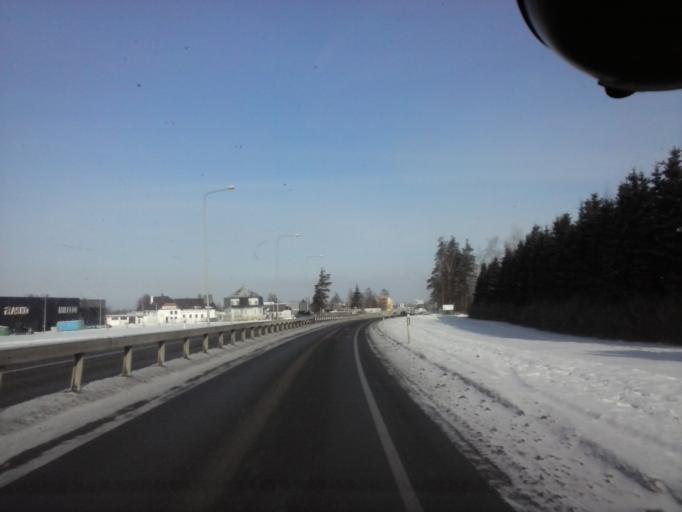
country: EE
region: Tartu
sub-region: Tartu linn
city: Tartu
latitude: 58.3615
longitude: 26.6779
